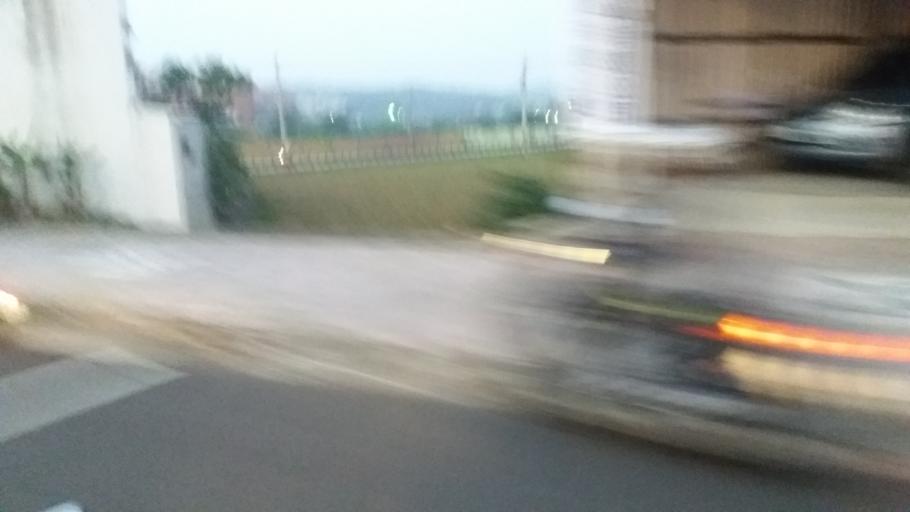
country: TW
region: Taiwan
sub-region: Hsinchu
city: Hsinchu
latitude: 24.7390
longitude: 120.9105
